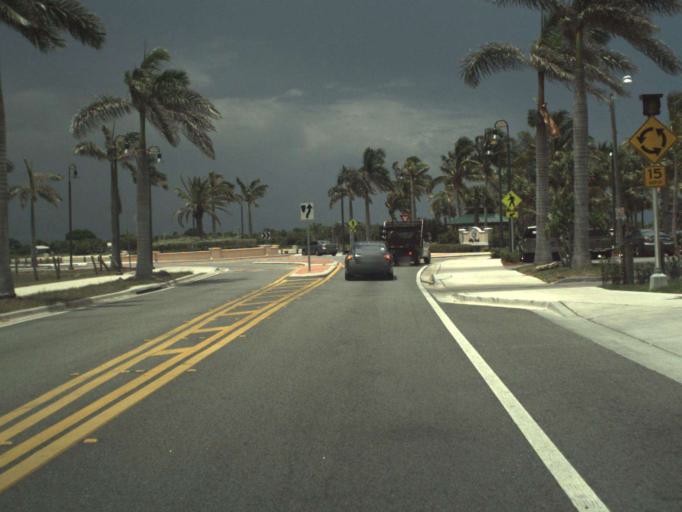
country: US
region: Florida
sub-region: Saint Lucie County
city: Fort Pierce
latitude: 27.4689
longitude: -80.2918
